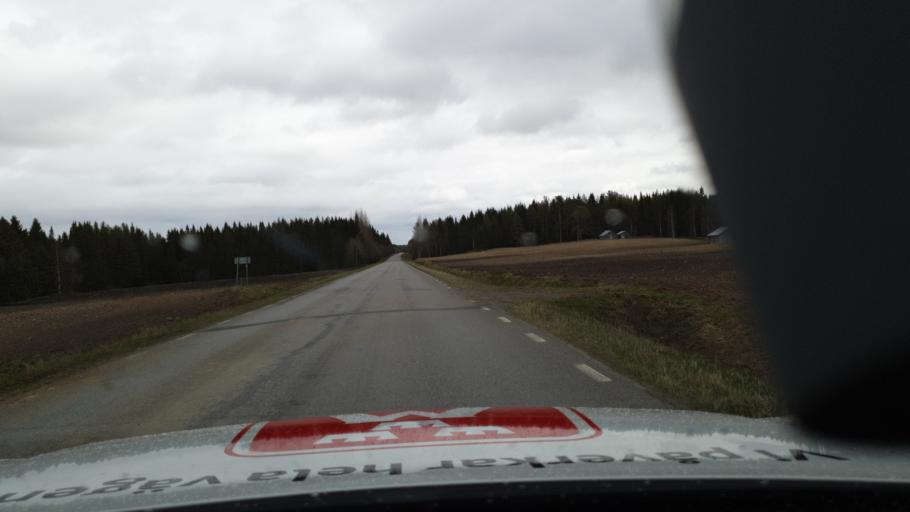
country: SE
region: Jaemtland
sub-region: Stroemsunds Kommun
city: Stroemsund
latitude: 63.6215
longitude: 15.2562
